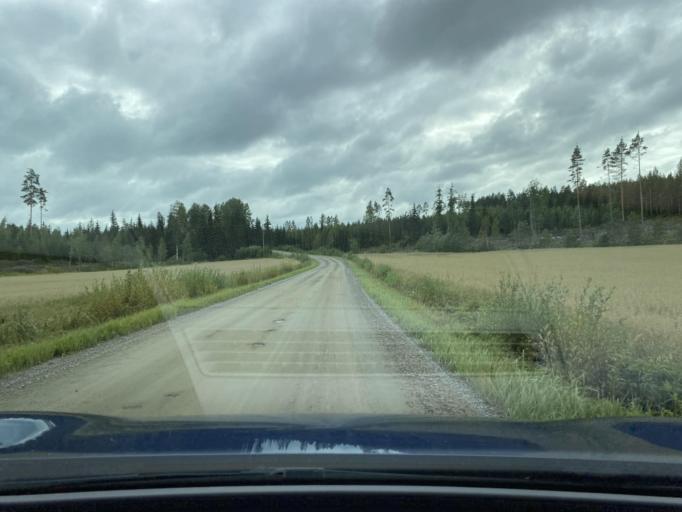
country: FI
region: Pirkanmaa
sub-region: Lounais-Pirkanmaa
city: Punkalaidun
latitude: 61.2146
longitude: 23.1691
